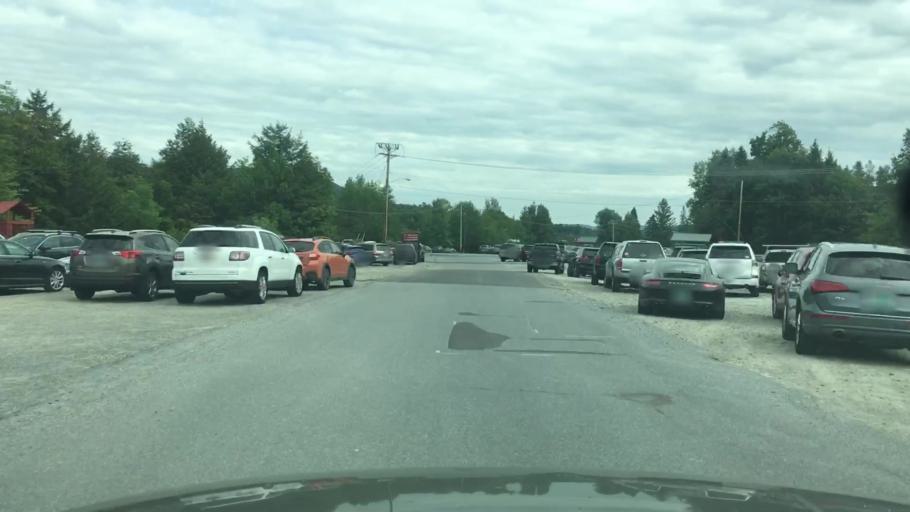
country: US
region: Vermont
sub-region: Windham County
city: Dover
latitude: 42.9700
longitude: -72.8952
